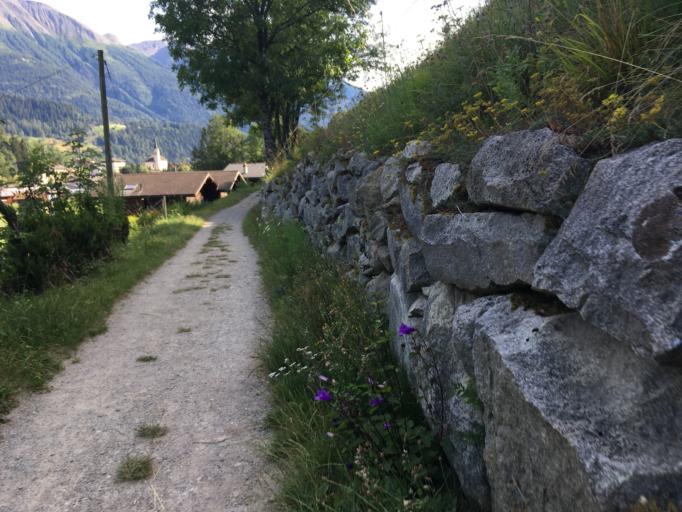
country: CH
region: Valais
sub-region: Goms District
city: Fiesch
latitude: 46.4103
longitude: 8.1369
